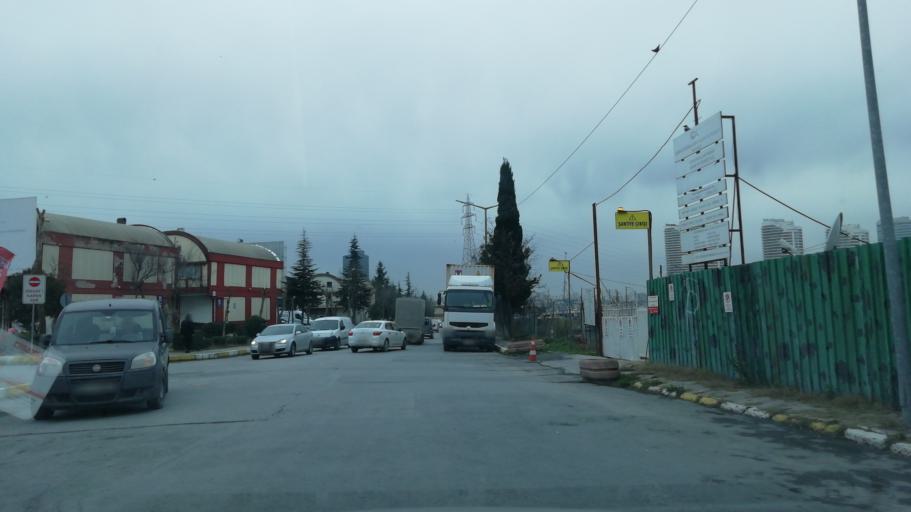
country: TR
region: Istanbul
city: Mahmutbey
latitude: 41.0677
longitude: 28.8187
